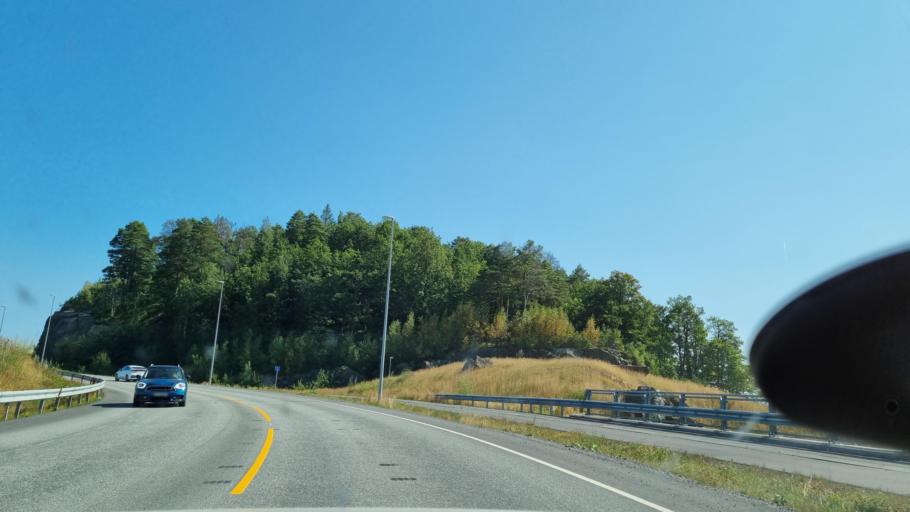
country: NO
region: Aust-Agder
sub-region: Arendal
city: Arendal
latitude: 58.4745
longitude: 8.8190
